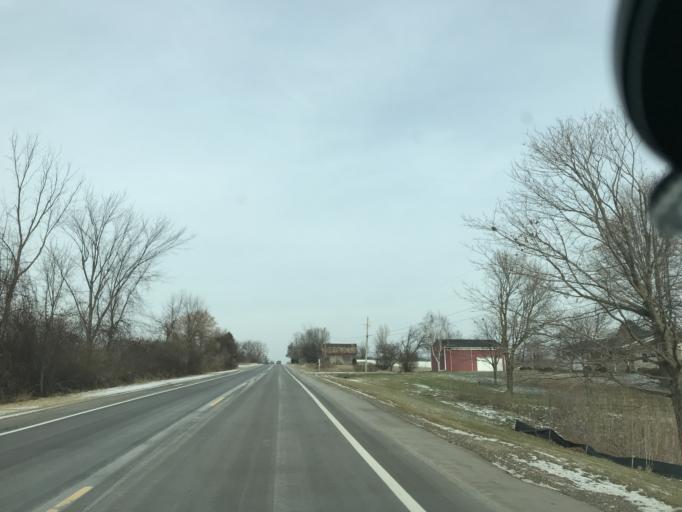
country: US
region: Michigan
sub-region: Ionia County
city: Lake Odessa
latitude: 42.7782
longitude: -85.0743
